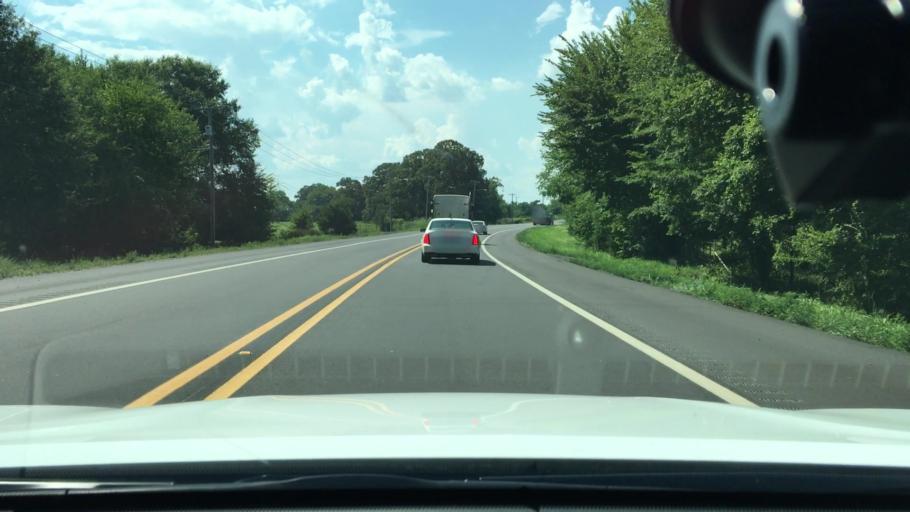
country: US
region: Arkansas
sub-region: Johnson County
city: Clarksville
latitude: 35.4535
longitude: -93.5323
